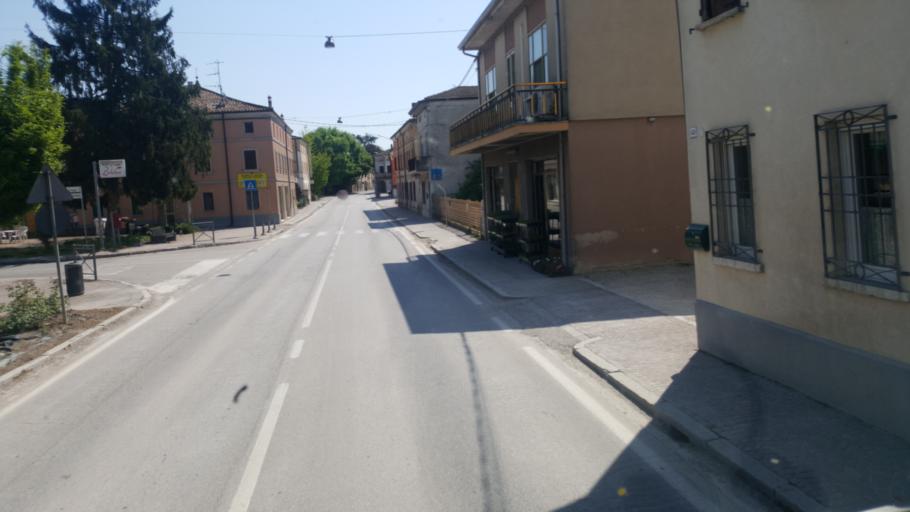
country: IT
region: Lombardy
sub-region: Provincia di Mantova
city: Sustinente
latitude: 45.0692
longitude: 11.0192
